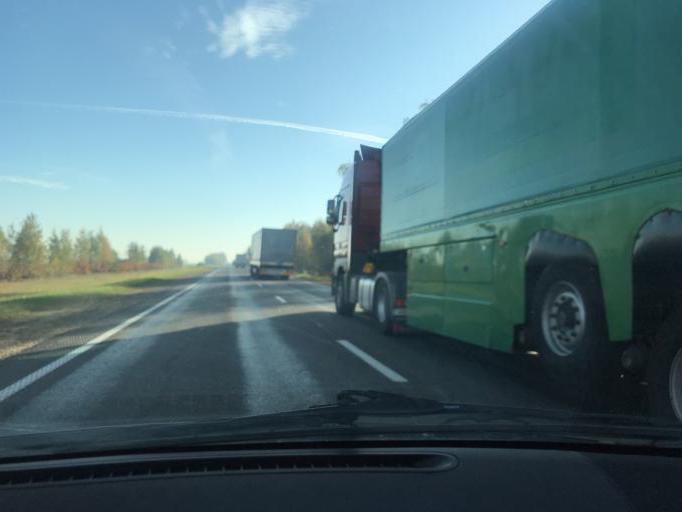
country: BY
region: Brest
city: Ivanava
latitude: 52.1482
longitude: 25.4211
